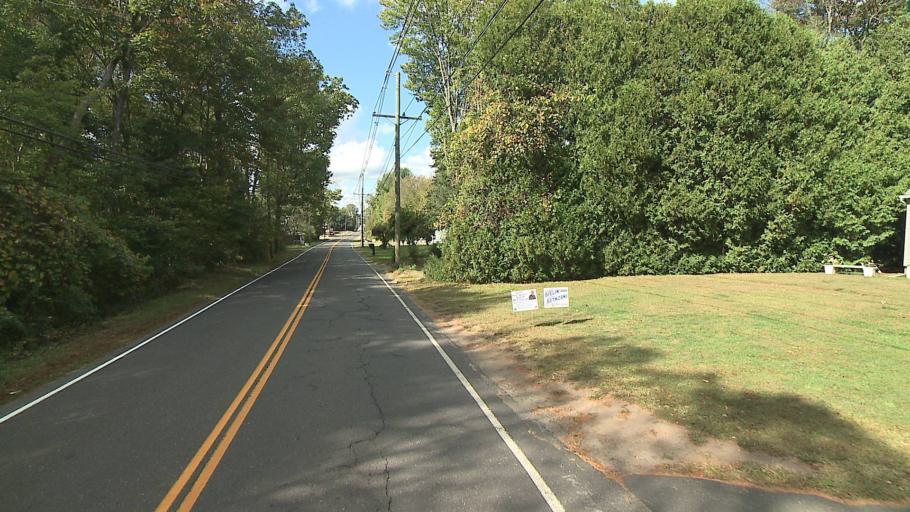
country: US
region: Connecticut
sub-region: New Haven County
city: Naugatuck
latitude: 41.4389
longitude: -73.0413
